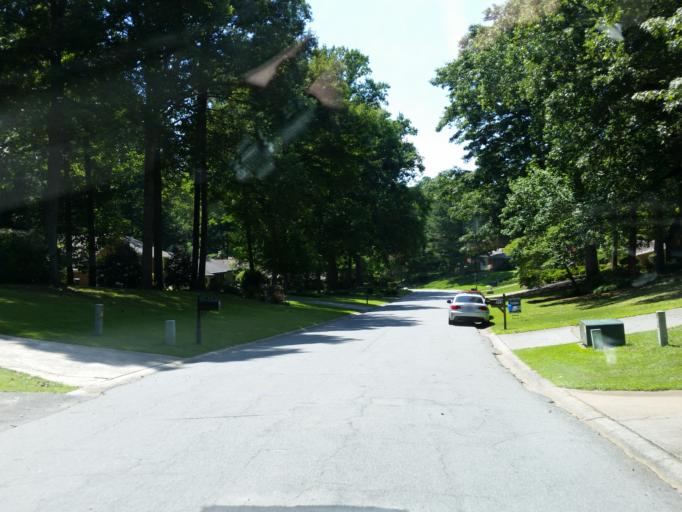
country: US
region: Georgia
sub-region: Cobb County
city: Marietta
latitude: 33.9561
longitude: -84.4896
